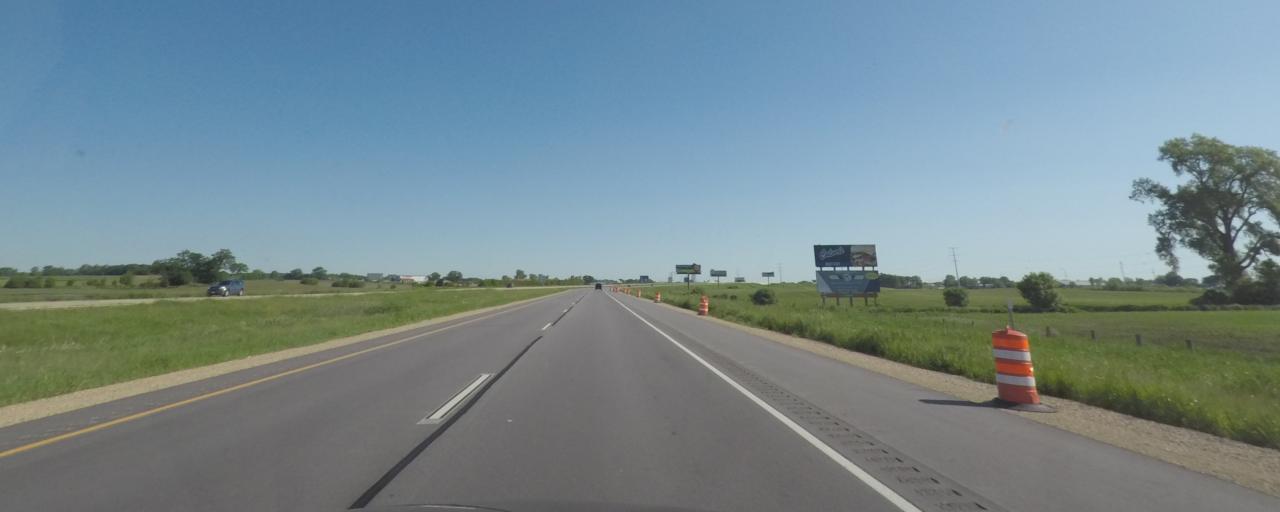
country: US
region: Wisconsin
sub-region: Columbia County
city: Columbus
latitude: 43.3338
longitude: -89.0442
